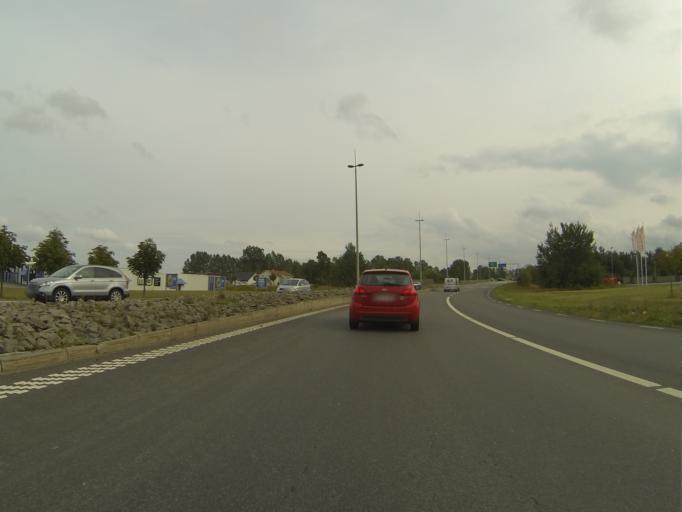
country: SE
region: Skane
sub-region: Kristianstads Kommun
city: Kristianstad
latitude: 56.0216
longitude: 14.1158
